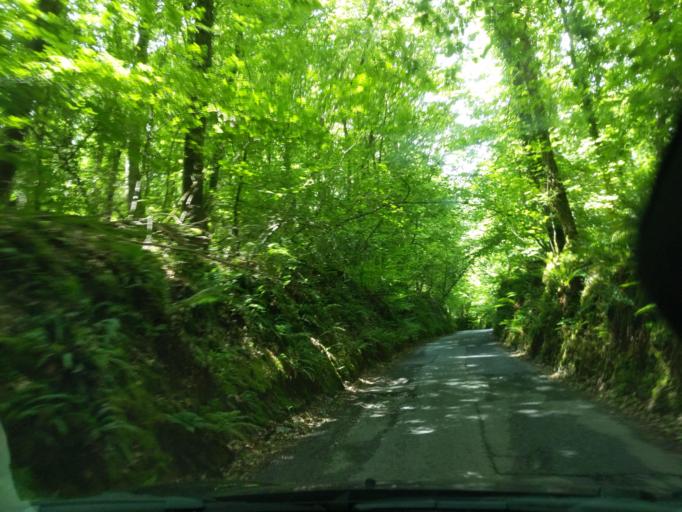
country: GB
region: England
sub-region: Devon
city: Plympton
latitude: 50.4123
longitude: -4.0795
